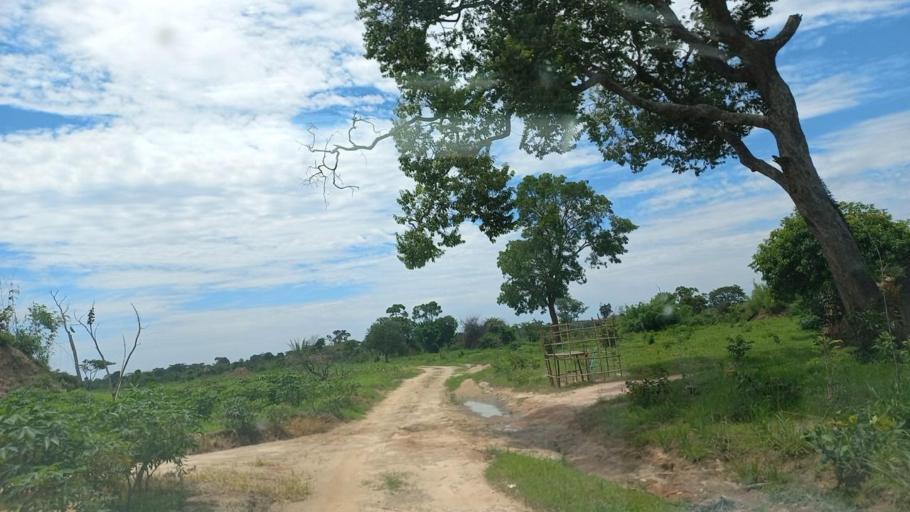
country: ZM
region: Copperbelt
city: Kitwe
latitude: -12.8053
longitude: 28.4010
